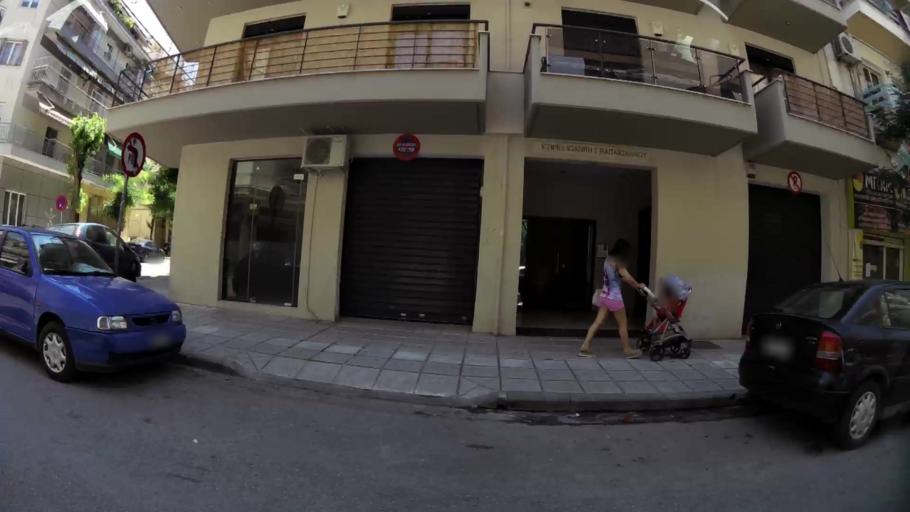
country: GR
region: Central Macedonia
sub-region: Nomos Thessalonikis
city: Triandria
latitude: 40.6101
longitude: 22.9599
